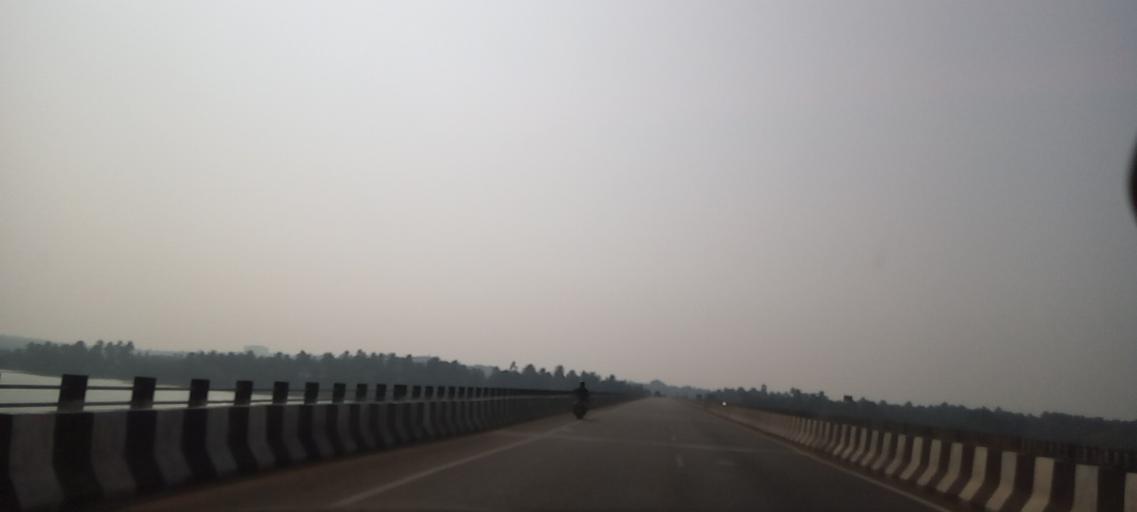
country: IN
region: Karnataka
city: Gangolli
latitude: 13.6848
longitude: 74.6822
